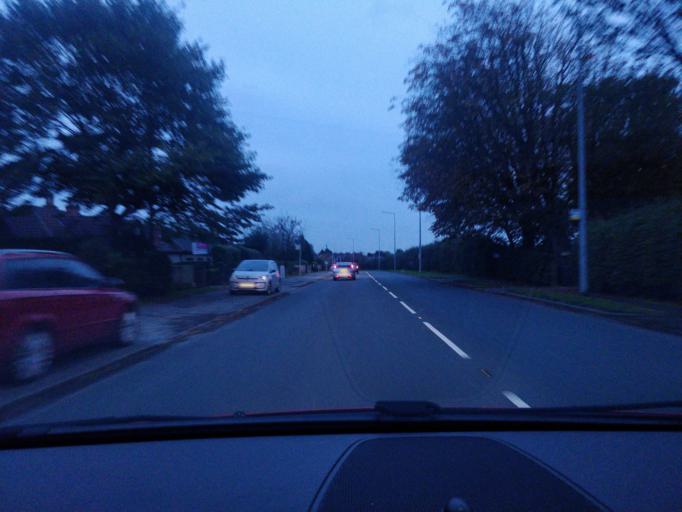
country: GB
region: England
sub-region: Lancashire
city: Ormskirk
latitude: 53.5766
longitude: -2.8948
